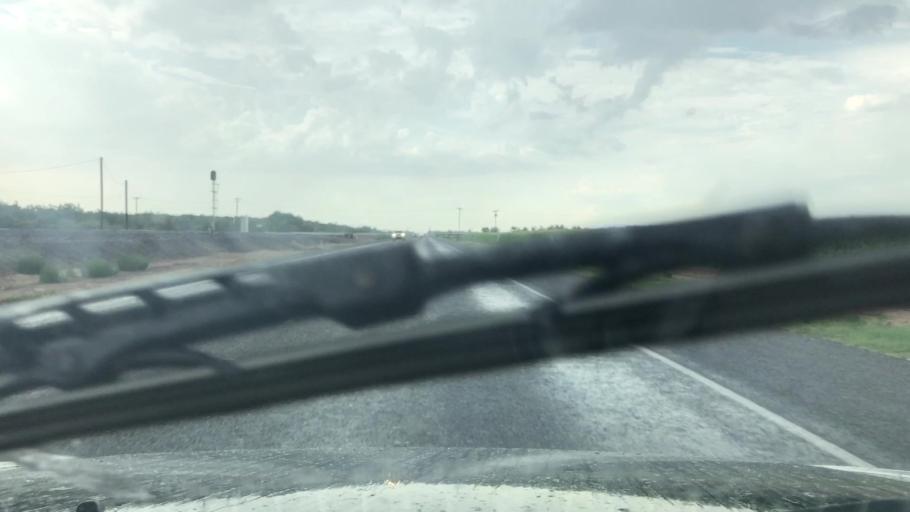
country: US
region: New Mexico
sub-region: Dona Ana County
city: Mesquite
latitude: 32.1436
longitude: -106.6833
